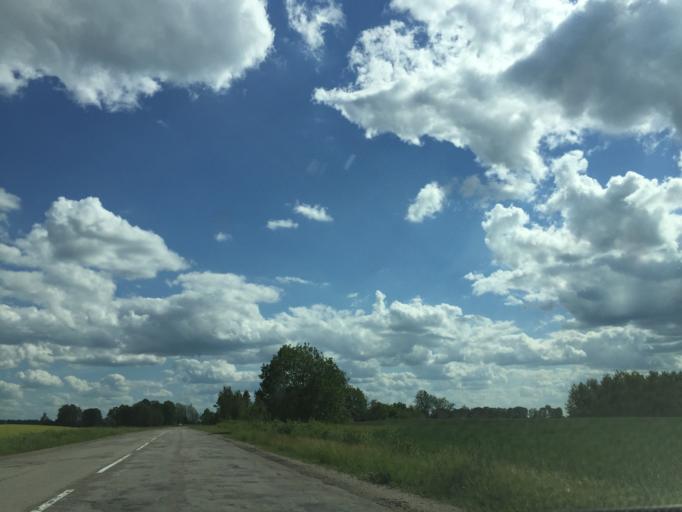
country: LV
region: Tukuma Rajons
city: Tukums
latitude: 56.8940
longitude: 23.0826
